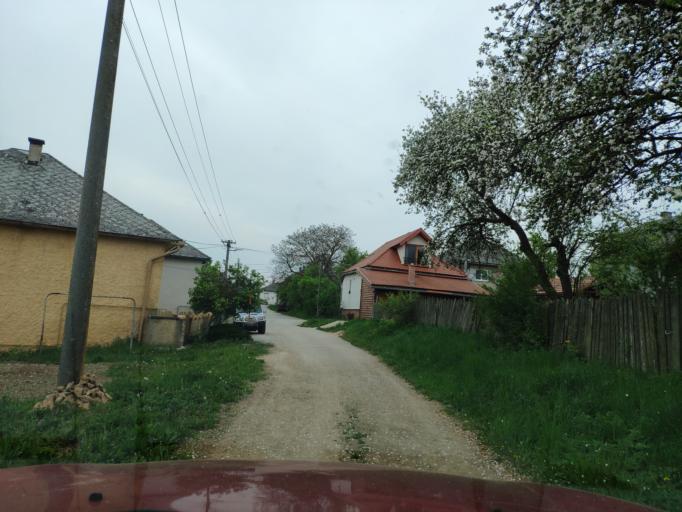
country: SK
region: Kosicky
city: Roznava
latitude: 48.5569
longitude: 20.5192
